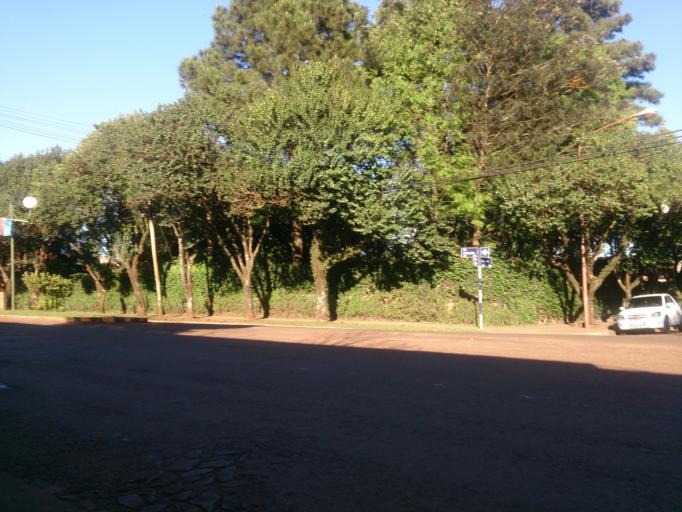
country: AR
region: Misiones
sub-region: Departamento de Obera
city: Obera
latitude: -27.4905
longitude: -55.1104
